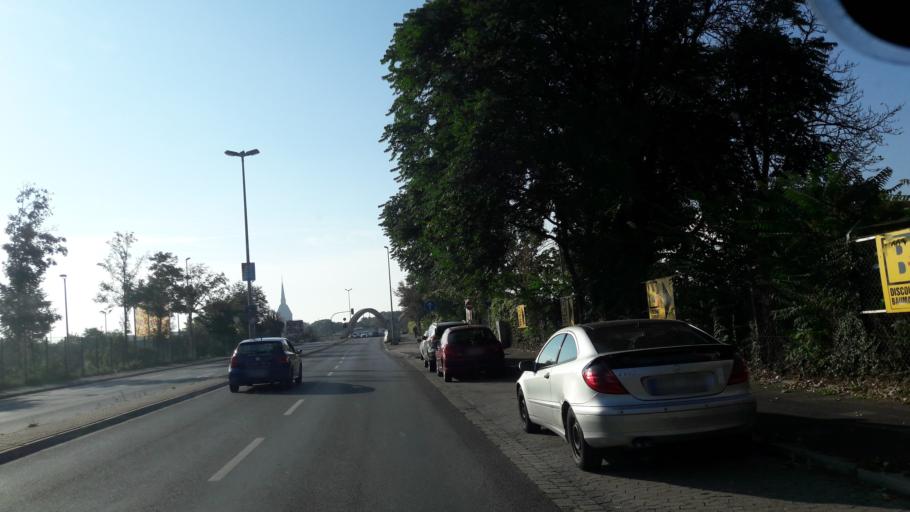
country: DE
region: Lower Saxony
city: Hildesheim
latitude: 52.1587
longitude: 9.9390
